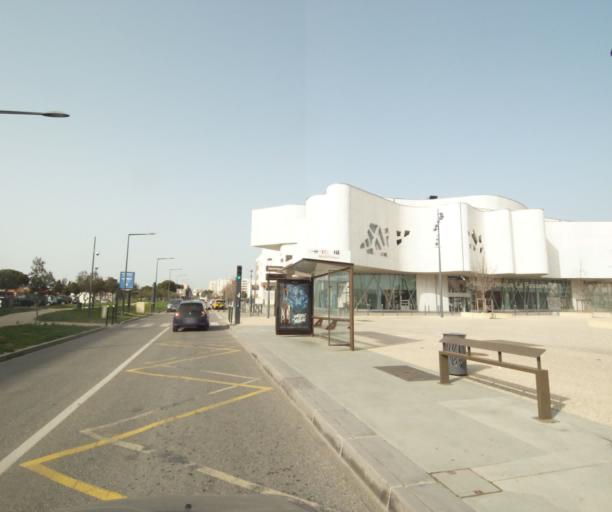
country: FR
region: Provence-Alpes-Cote d'Azur
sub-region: Departement des Bouches-du-Rhone
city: Vitrolles
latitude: 43.4427
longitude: 5.2525
